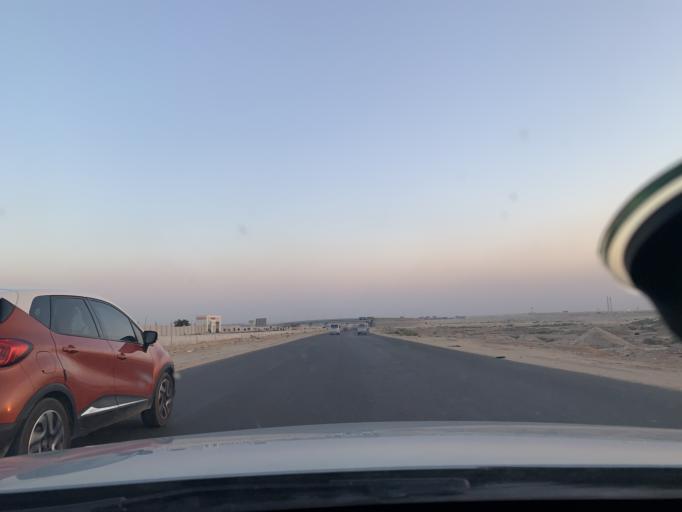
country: EG
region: Muhafazat al Qalyubiyah
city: Al Khankah
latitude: 30.2177
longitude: 31.4246
